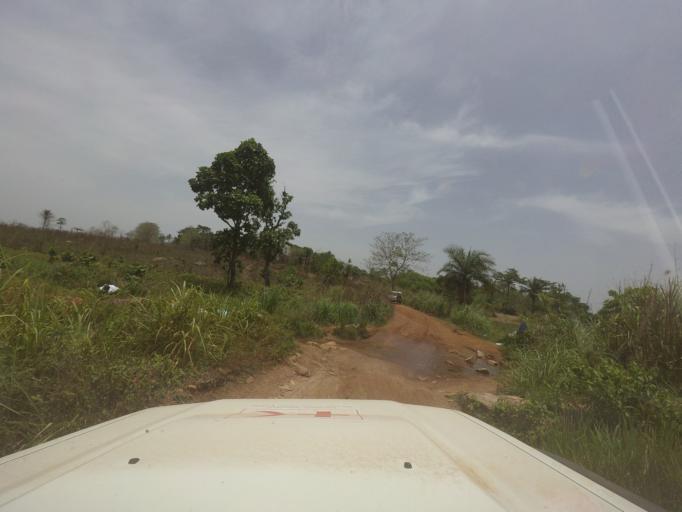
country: SL
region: Eastern Province
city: Buedu
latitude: 8.4894
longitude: -10.3329
